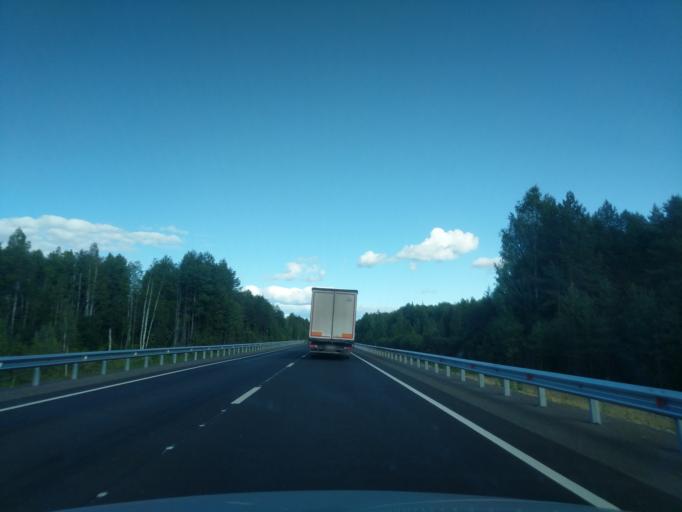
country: RU
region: Kostroma
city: Makar'yev
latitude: 57.8480
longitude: 43.6652
